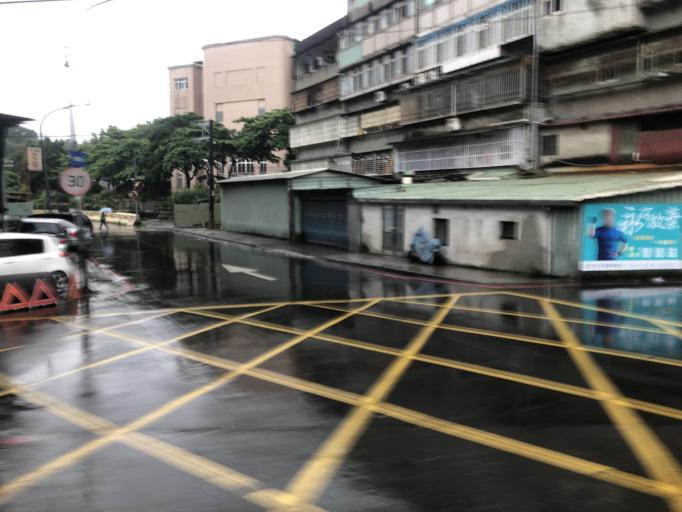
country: TW
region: Taipei
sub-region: Taipei
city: Banqiao
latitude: 24.9639
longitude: 121.4290
